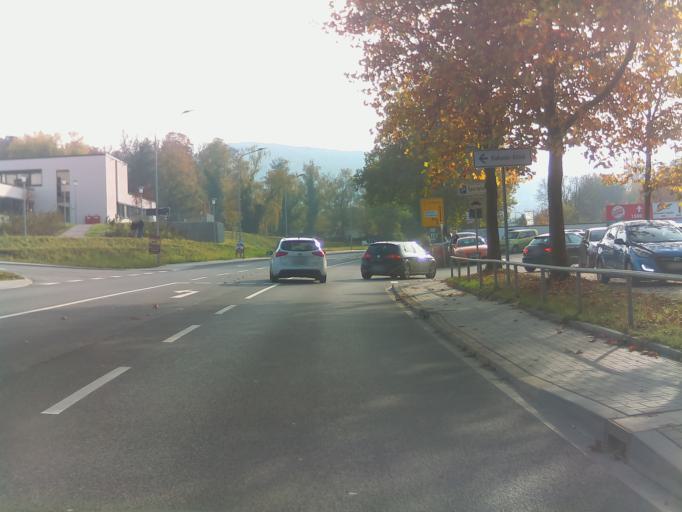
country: DE
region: Baden-Wuerttemberg
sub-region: Karlsruhe Region
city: Mosbach
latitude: 49.3634
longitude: 9.1517
